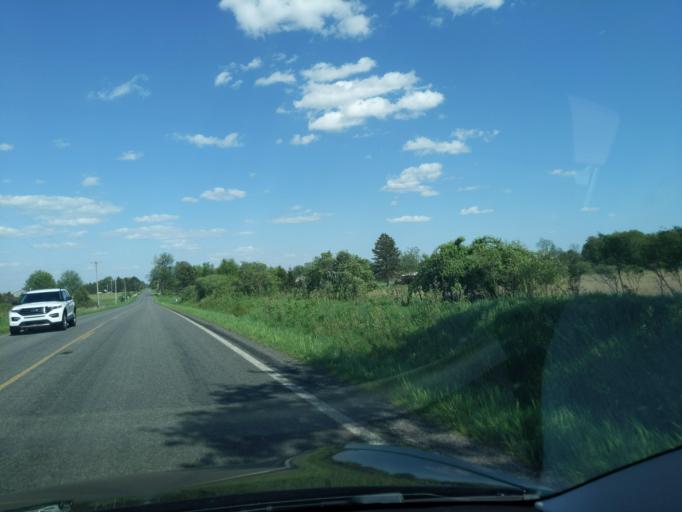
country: US
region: Michigan
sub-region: Ionia County
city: Lake Odessa
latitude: 42.7843
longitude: -85.1895
